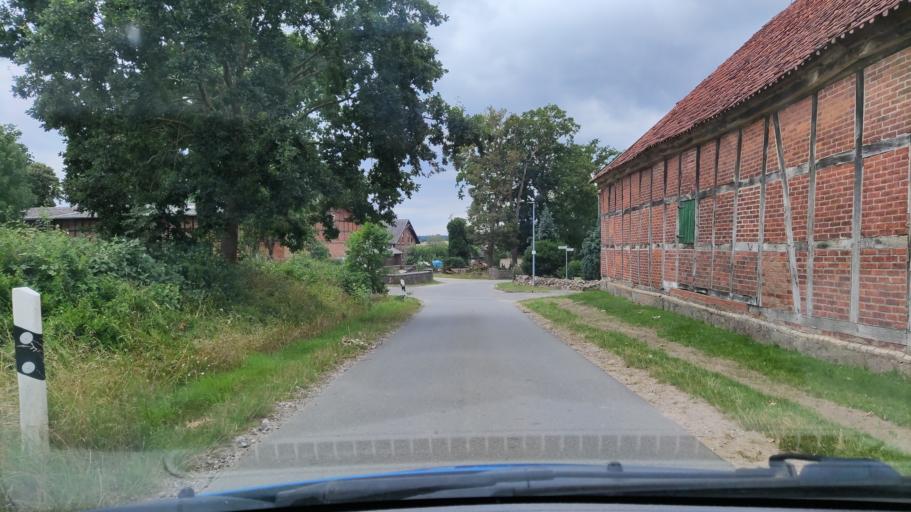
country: DE
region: Lower Saxony
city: Romstedt
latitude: 53.1031
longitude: 10.6564
